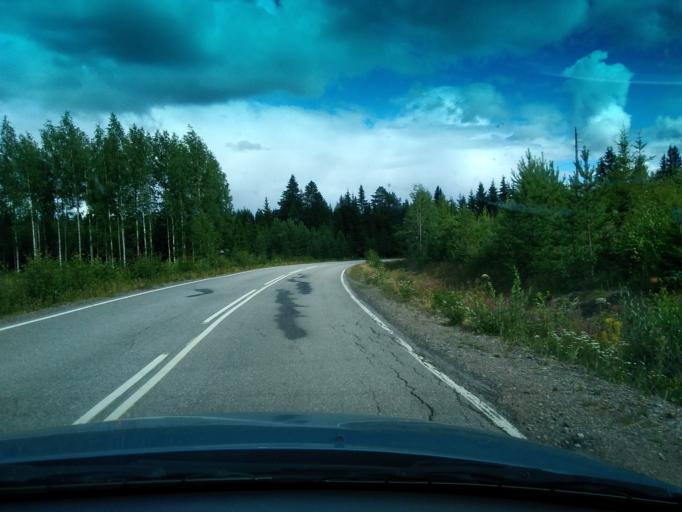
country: FI
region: Central Finland
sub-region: Saarijaervi-Viitasaari
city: Saarijaervi
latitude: 62.7339
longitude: 25.1482
